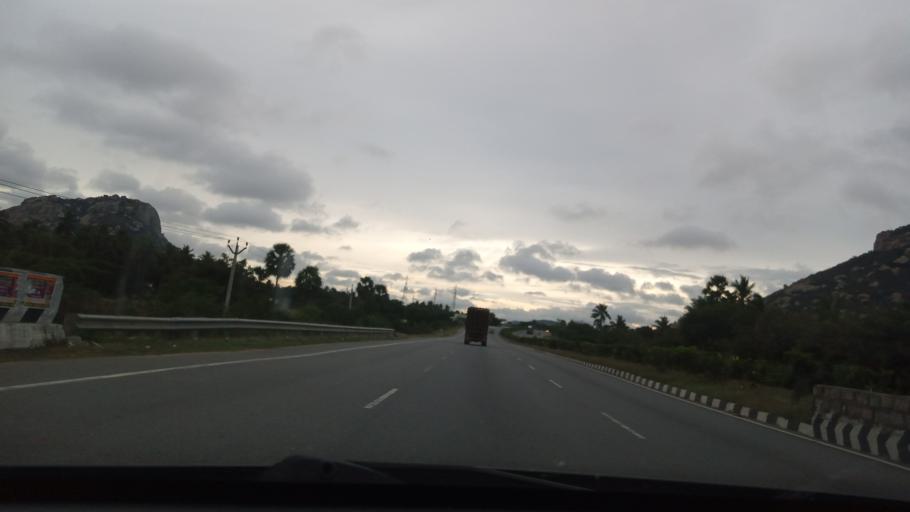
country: IN
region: Tamil Nadu
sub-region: Vellore
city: Jolarpettai
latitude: 12.5594
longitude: 78.4619
